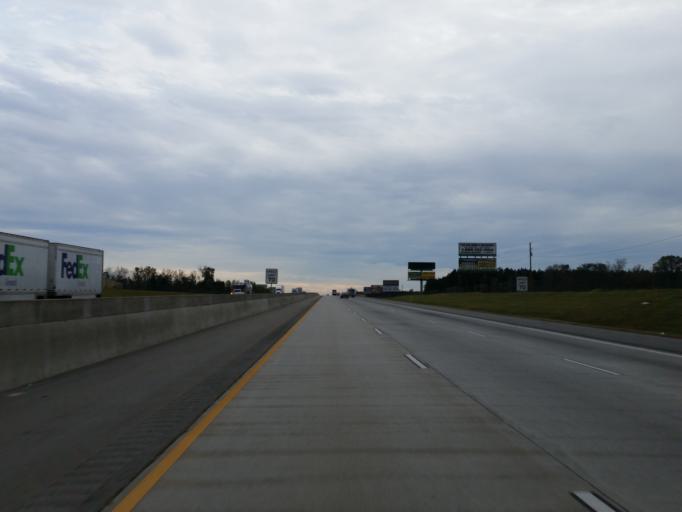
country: US
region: Georgia
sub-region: Tift County
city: Unionville
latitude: 31.4019
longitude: -83.5012
